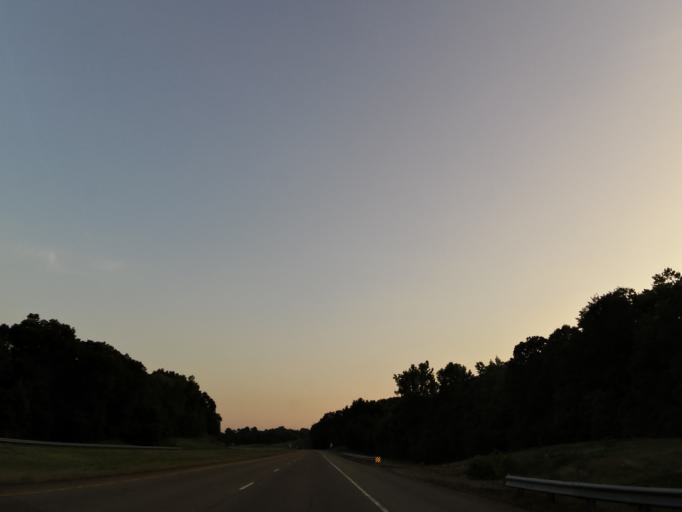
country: US
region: Tennessee
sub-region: Henry County
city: Paris
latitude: 36.2072
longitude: -88.4034
